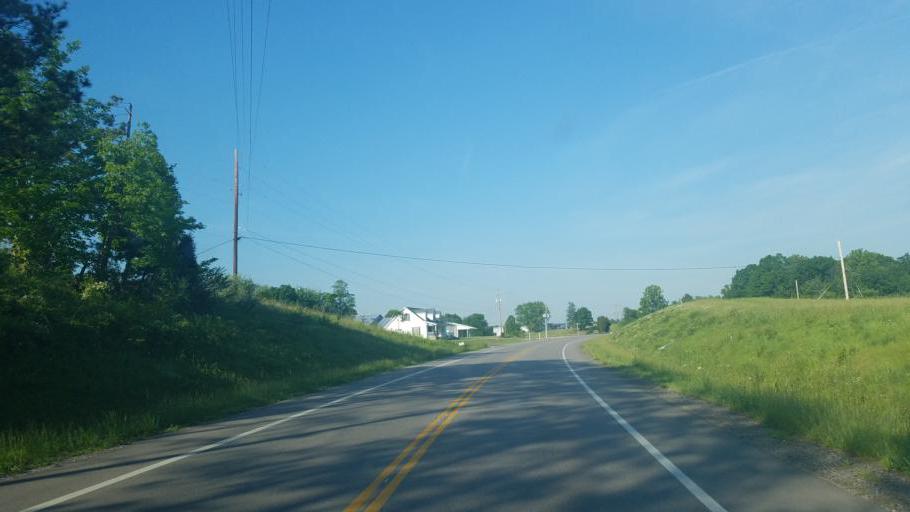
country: US
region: West Virginia
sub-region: Mason County
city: New Haven
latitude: 39.1372
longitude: -81.8590
